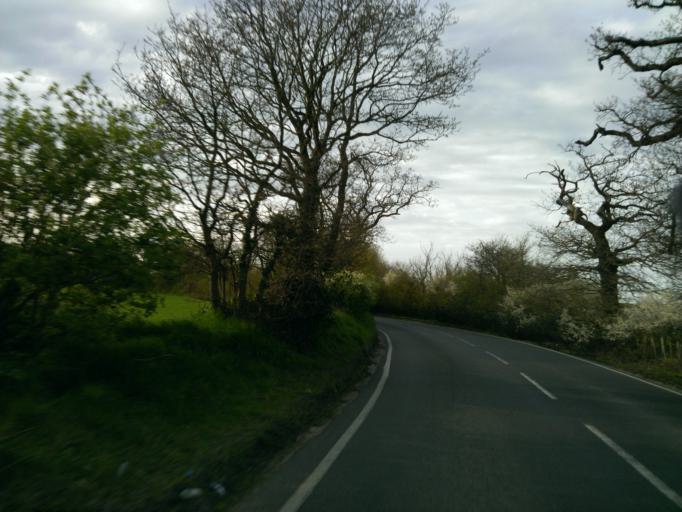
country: GB
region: England
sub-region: Essex
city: Wivenhoe
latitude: 51.8591
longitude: 0.9759
